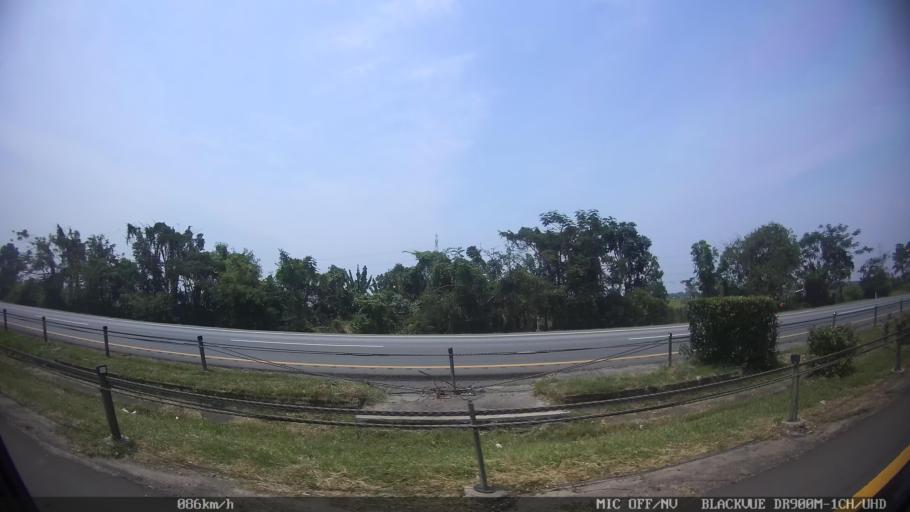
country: ID
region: Banten
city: Serang
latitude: -6.0486
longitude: 106.1145
